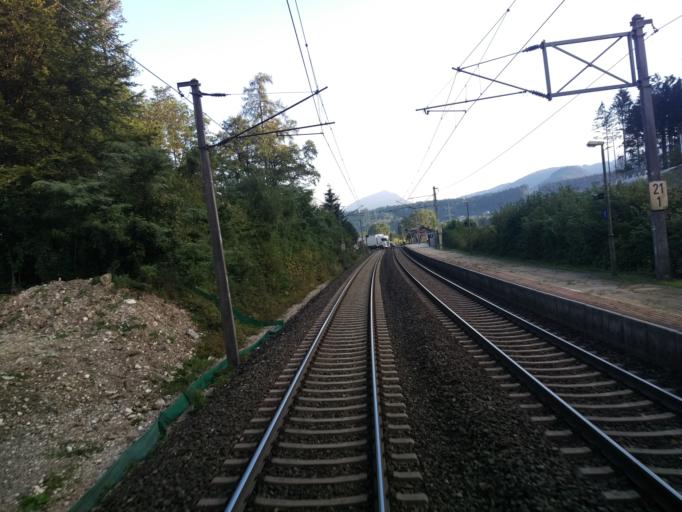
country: AT
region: Salzburg
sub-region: Politischer Bezirk Hallein
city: Adnet
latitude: 47.6628
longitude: 13.1236
